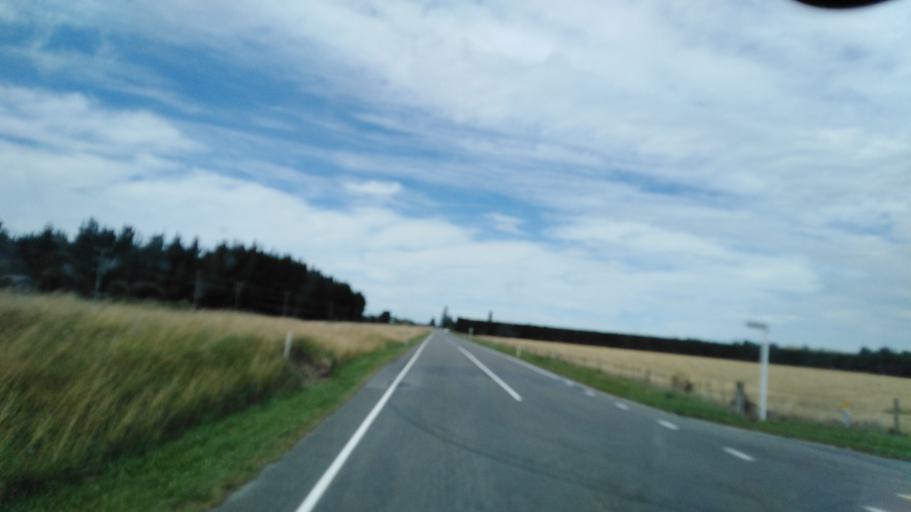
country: NZ
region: Canterbury
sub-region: Selwyn District
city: Darfield
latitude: -43.3775
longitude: 171.9996
